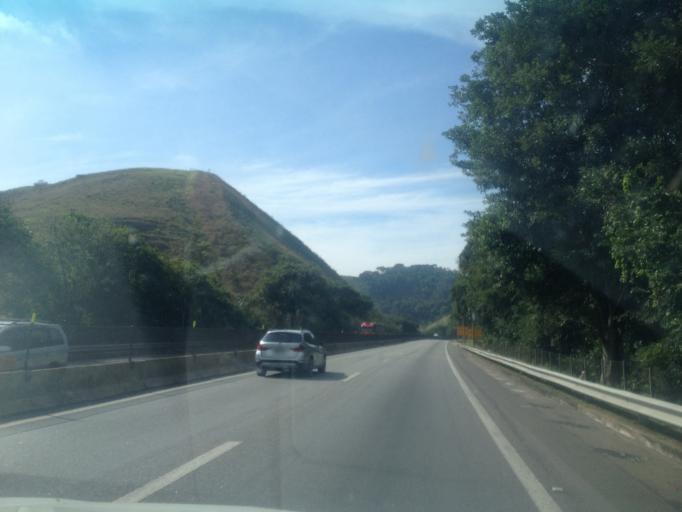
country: BR
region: Rio de Janeiro
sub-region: Pirai
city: Pirai
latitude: -22.6650
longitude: -43.8767
